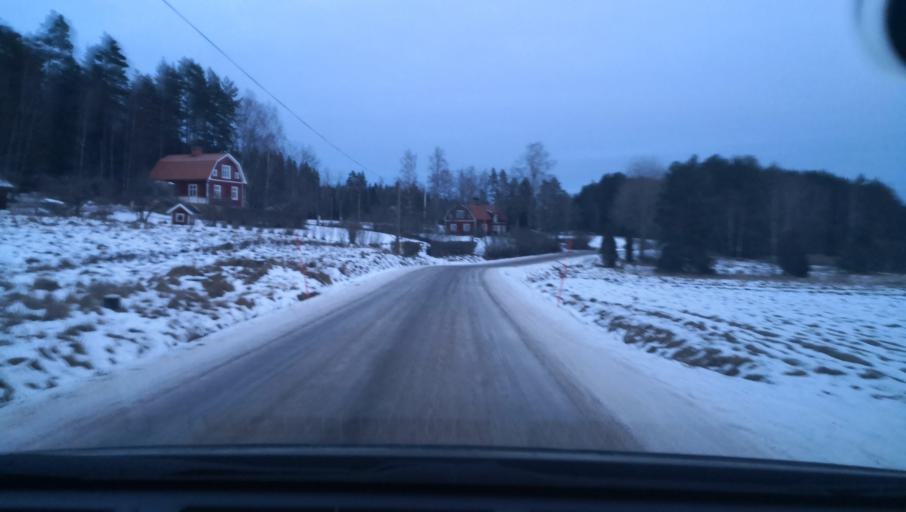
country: SE
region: Dalarna
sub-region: Avesta Kommun
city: Horndal
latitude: 60.2025
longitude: 16.5145
